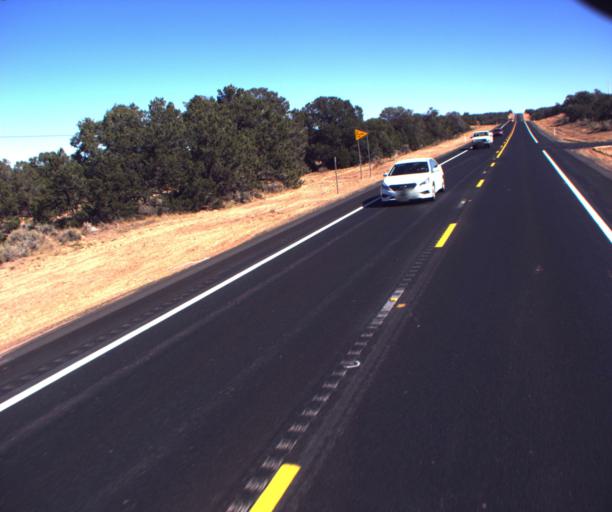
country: US
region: Arizona
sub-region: Apache County
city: Ganado
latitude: 35.7183
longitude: -109.3917
